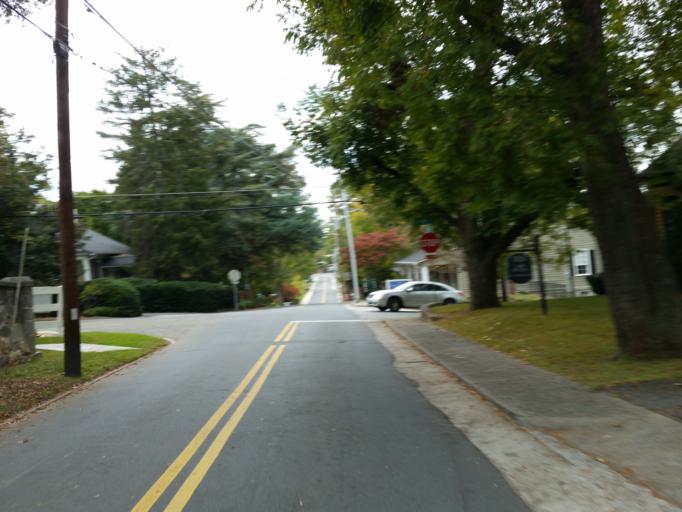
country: US
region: Georgia
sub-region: Cobb County
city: Marietta
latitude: 33.9522
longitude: -84.5432
